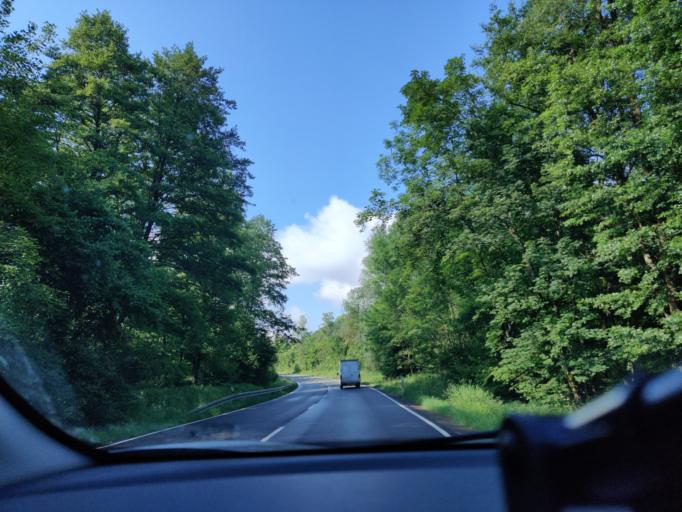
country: DE
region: Saarland
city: Gersheim
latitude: 49.1577
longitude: 7.1555
